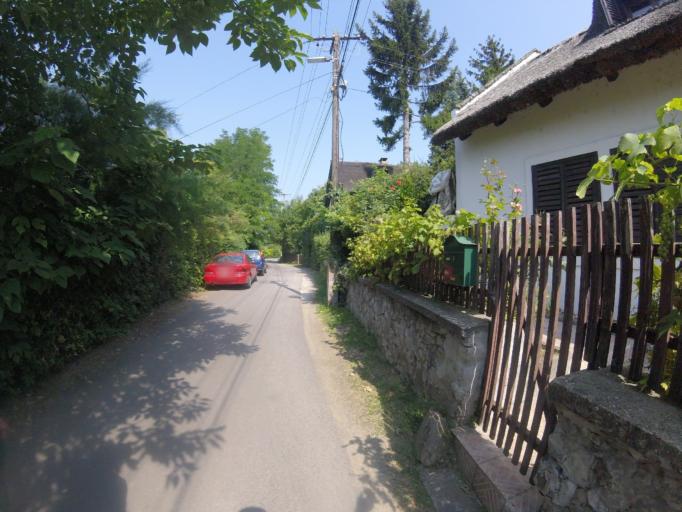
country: HU
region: Veszprem
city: Badacsonytomaj
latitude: 46.8021
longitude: 17.4358
